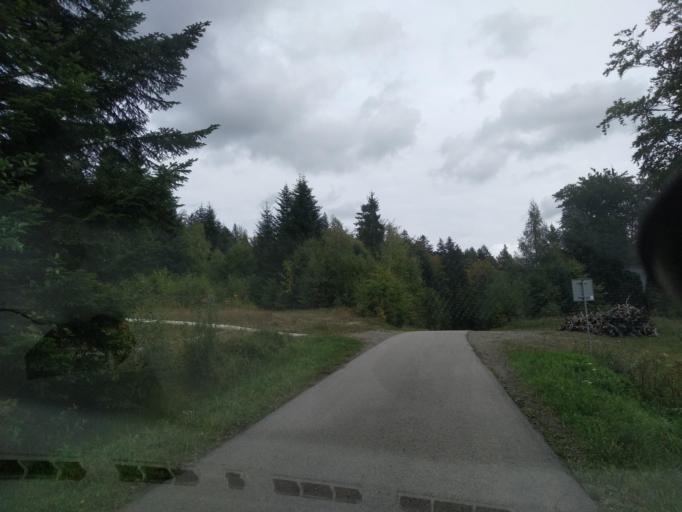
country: PL
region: Lesser Poland Voivodeship
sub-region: Powiat gorlicki
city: Sekowa
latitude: 49.5434
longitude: 21.2277
